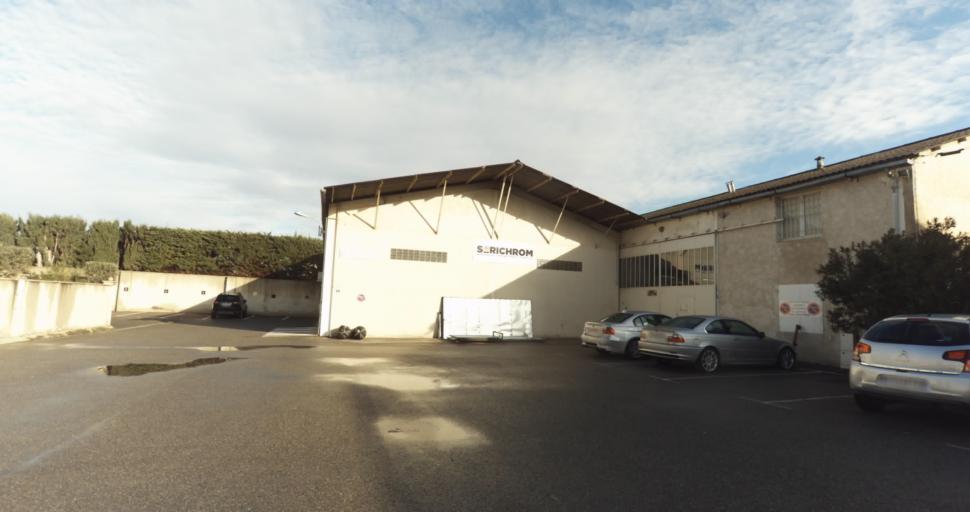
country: FR
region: Provence-Alpes-Cote d'Azur
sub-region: Departement des Bouches-du-Rhone
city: Rognonas
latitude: 43.9022
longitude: 4.8020
